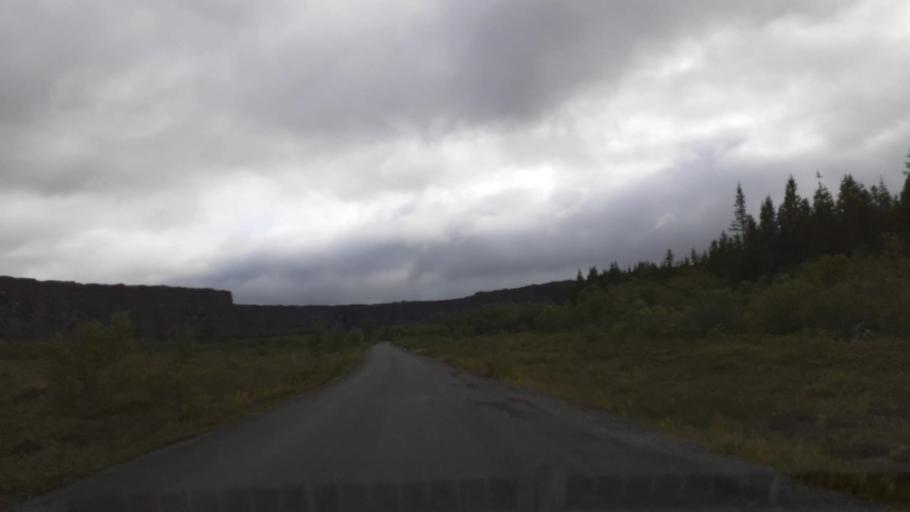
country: IS
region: Northeast
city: Husavik
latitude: 66.0105
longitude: -16.5066
